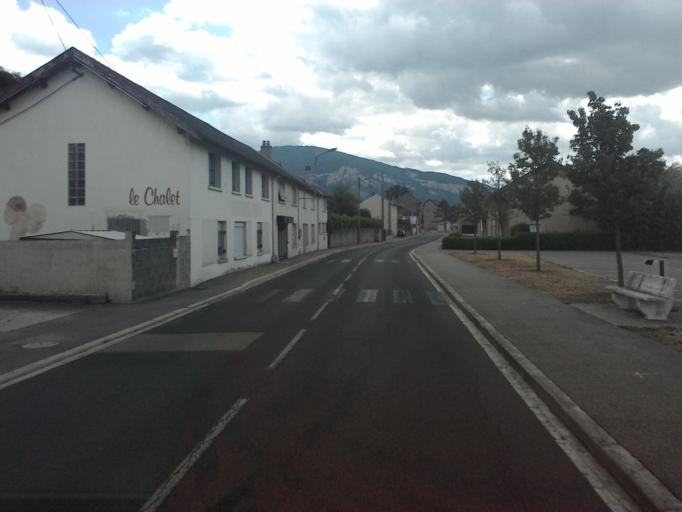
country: FR
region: Rhone-Alpes
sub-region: Departement de l'Ain
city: Sault-Brenaz
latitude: 45.8595
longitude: 5.4024
